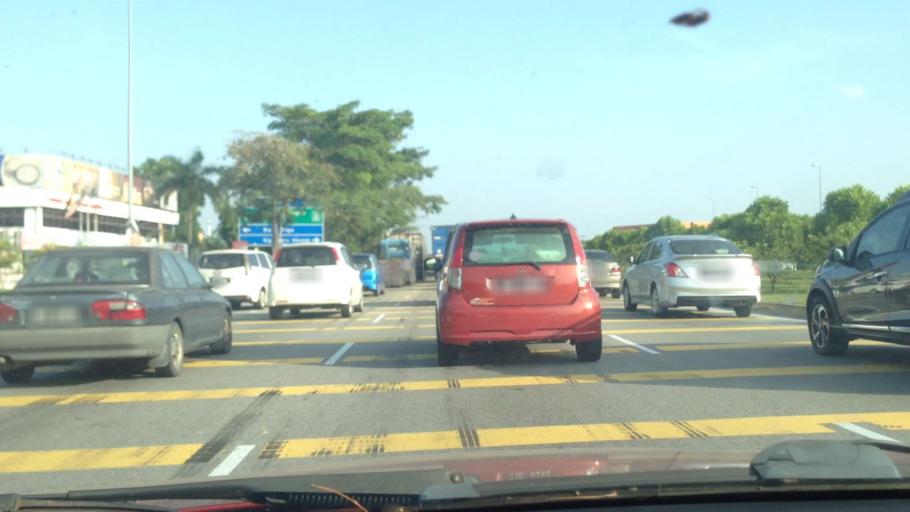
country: MY
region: Selangor
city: Subang Jaya
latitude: 3.0419
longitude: 101.5468
